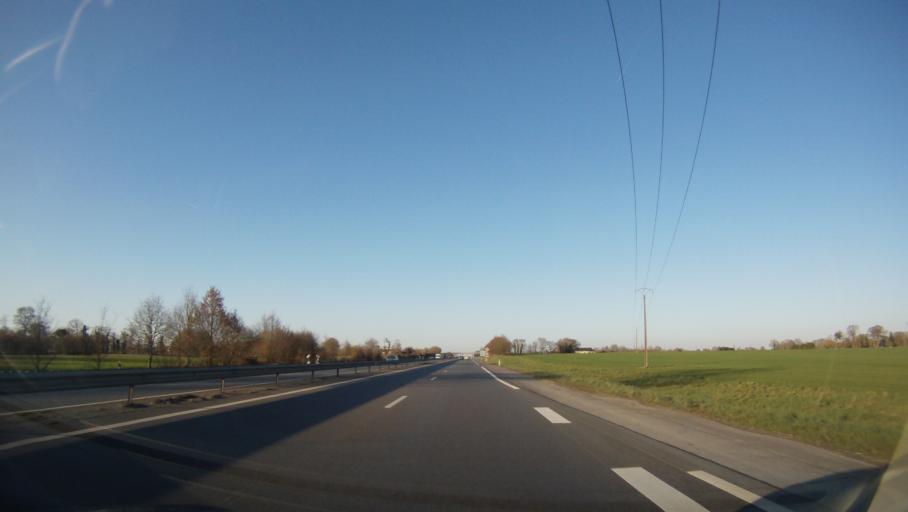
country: FR
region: Brittany
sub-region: Departement d'Ille-et-Vilaine
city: Chatillon-sur-Seiche
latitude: 48.0456
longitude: -1.6841
